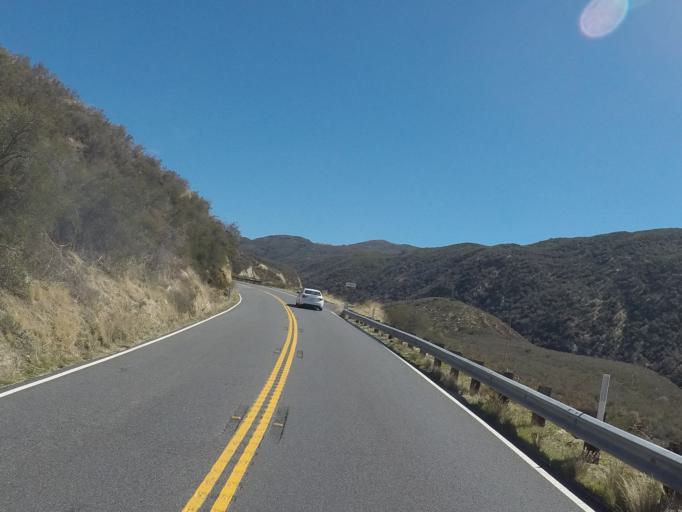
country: US
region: California
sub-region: Riverside County
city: Idyllwild-Pine Cove
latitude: 33.7121
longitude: -116.7790
